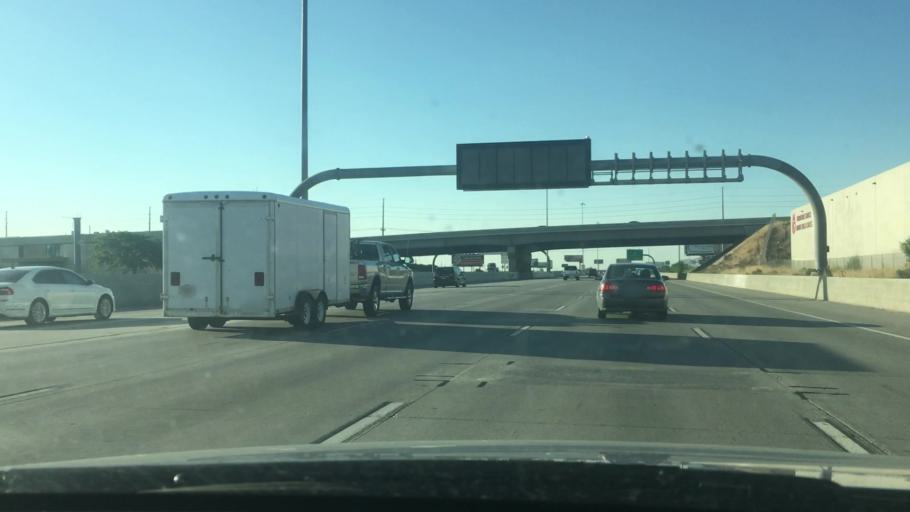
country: US
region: Utah
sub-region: Salt Lake County
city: Centerfield
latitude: 40.6854
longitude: -111.9024
